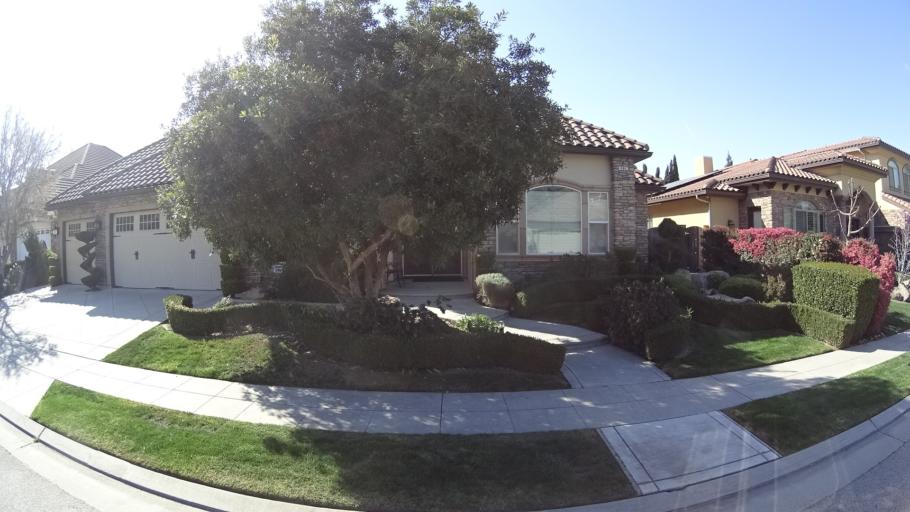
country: US
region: California
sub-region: Fresno County
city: Clovis
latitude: 36.8946
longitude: -119.7492
